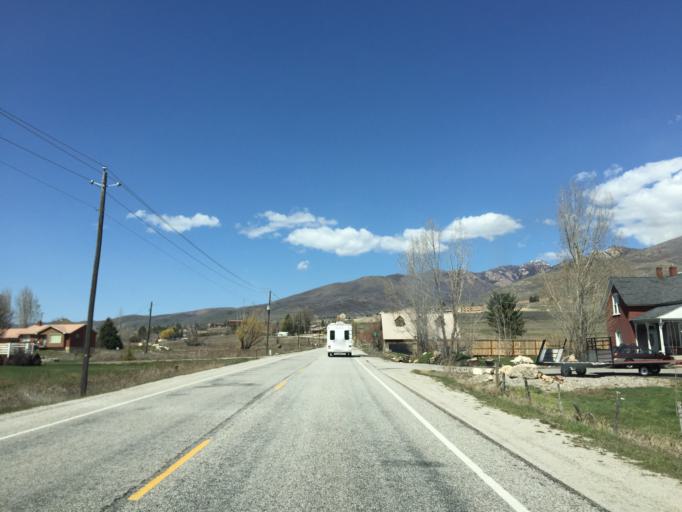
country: US
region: Utah
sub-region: Weber County
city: Wolf Creek
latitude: 41.3133
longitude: -111.8253
